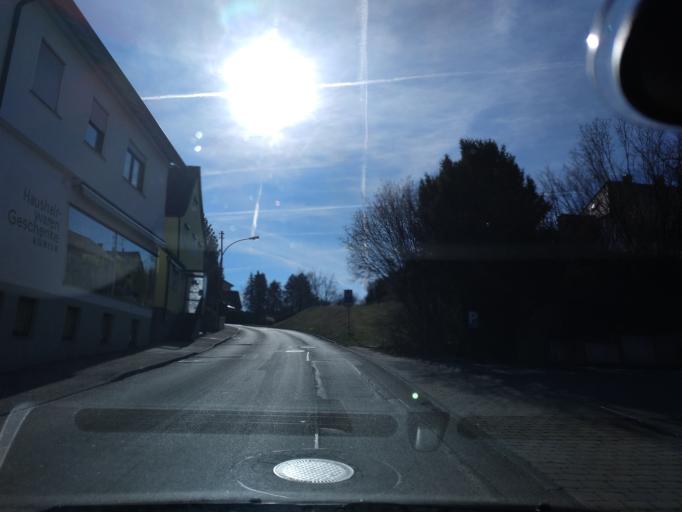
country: DE
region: Baden-Wuerttemberg
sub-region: Regierungsbezirk Stuttgart
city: Mainhardt
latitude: 49.0796
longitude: 9.5571
